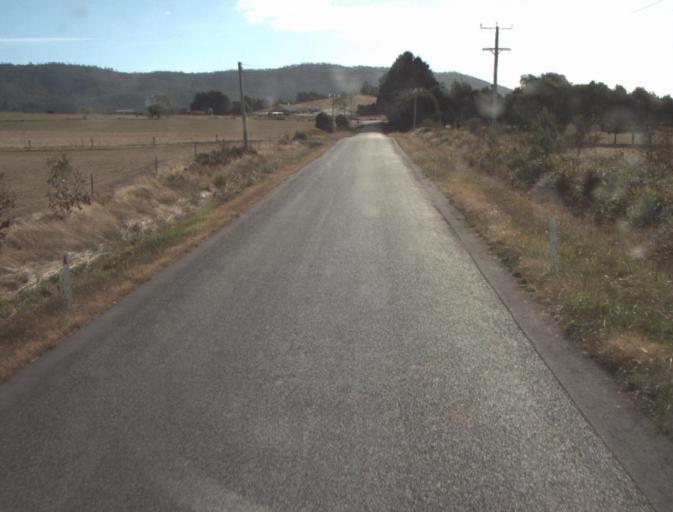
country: AU
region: Tasmania
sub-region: Launceston
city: Mayfield
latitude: -41.2373
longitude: 147.1542
